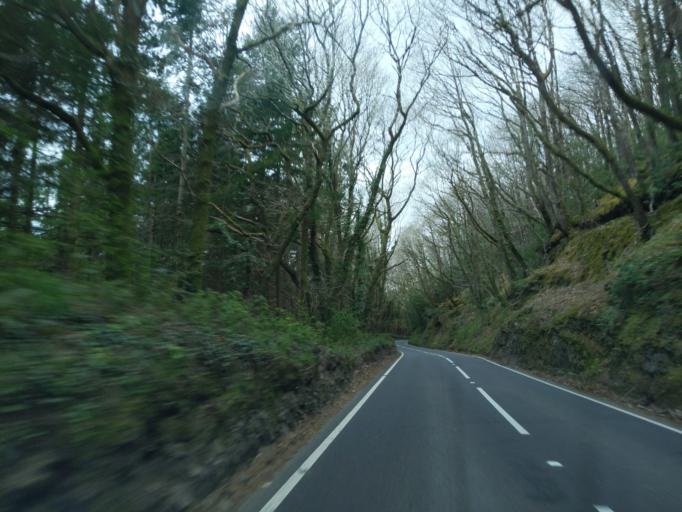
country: GB
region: England
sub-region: Devon
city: Great Torrington
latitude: 50.9338
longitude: -4.1144
